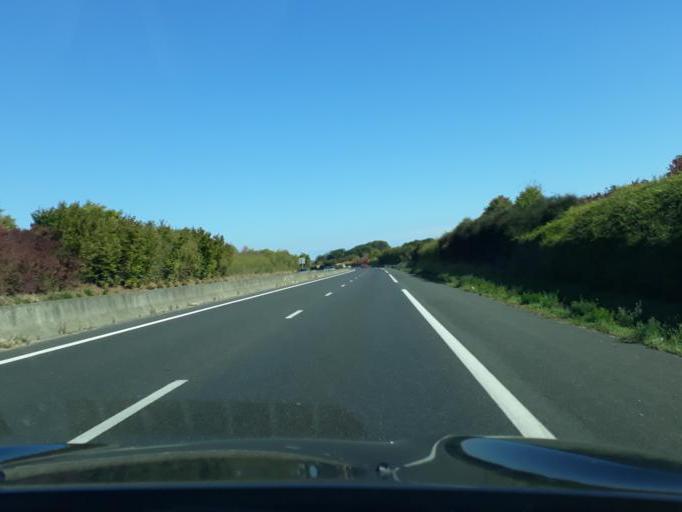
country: FR
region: Centre
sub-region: Departement d'Indre-et-Loire
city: Ballan-Mire
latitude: 47.3359
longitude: 0.6260
